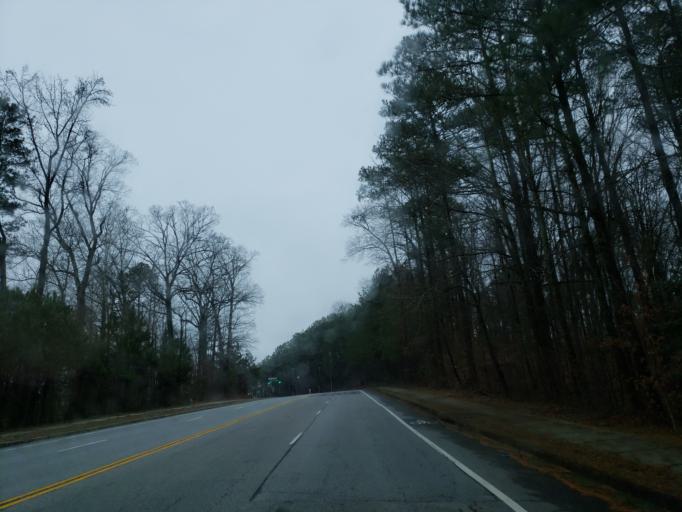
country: US
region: Georgia
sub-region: Fulton County
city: Roswell
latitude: 34.0157
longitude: -84.3245
